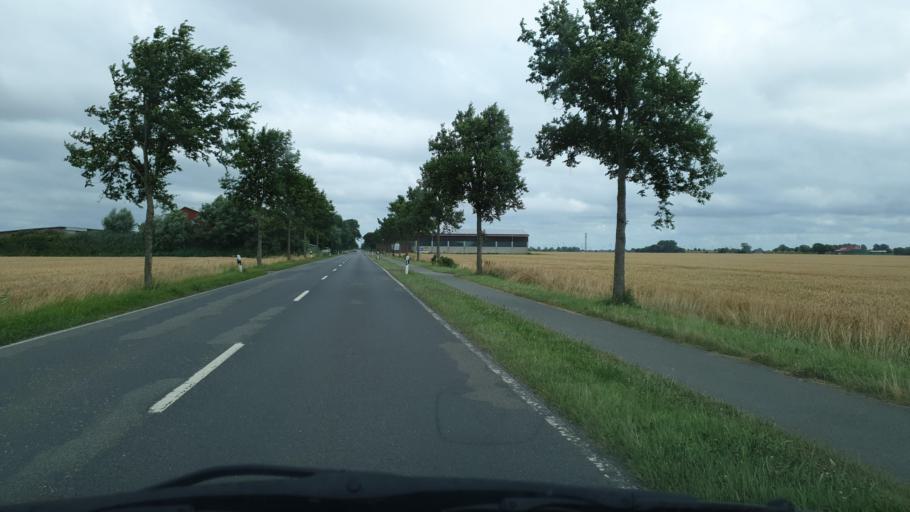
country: DE
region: Schleswig-Holstein
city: Friedrichskoog
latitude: 54.0281
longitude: 8.8479
